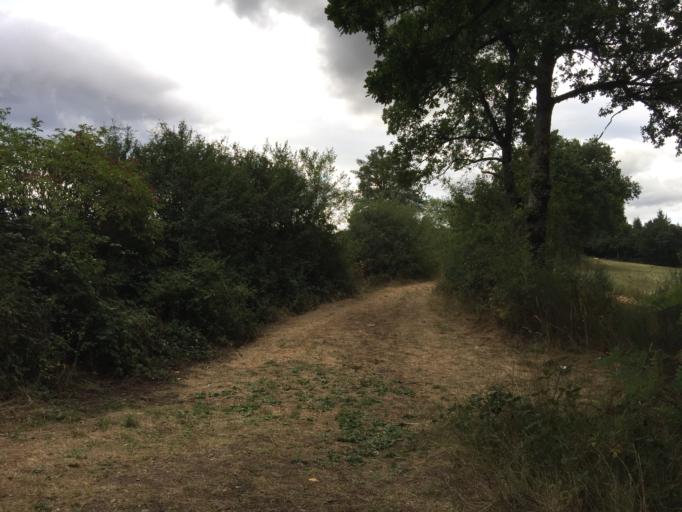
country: FR
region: Midi-Pyrenees
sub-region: Departement de l'Aveyron
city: Pont-de-Salars
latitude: 44.2942
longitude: 2.7295
